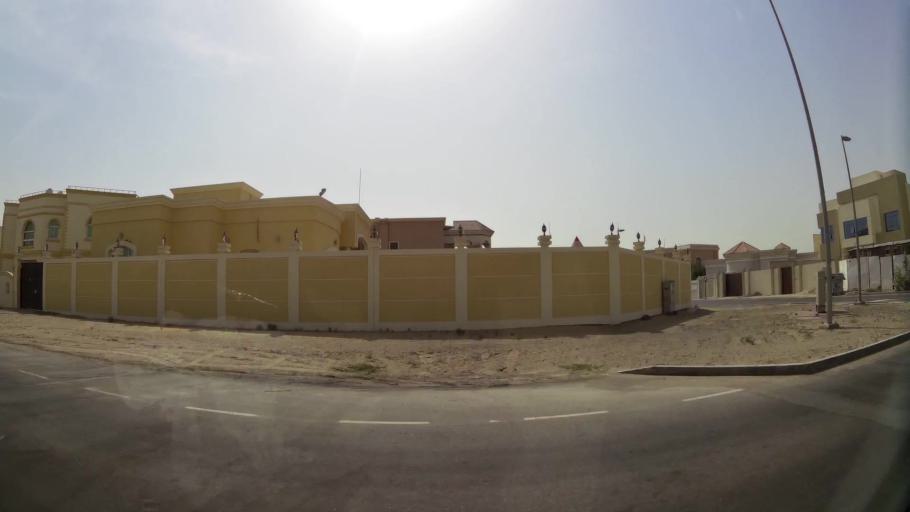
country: AE
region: Ash Shariqah
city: Sharjah
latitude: 25.2622
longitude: 55.4684
